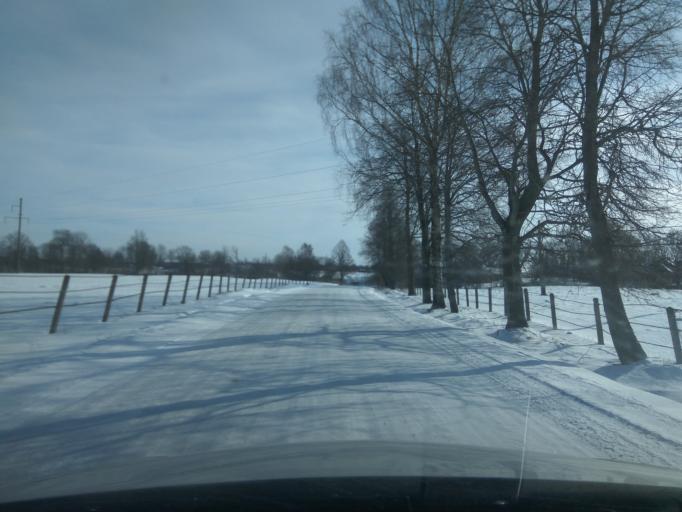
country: LV
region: Kuldigas Rajons
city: Kuldiga
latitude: 56.9897
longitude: 21.9502
